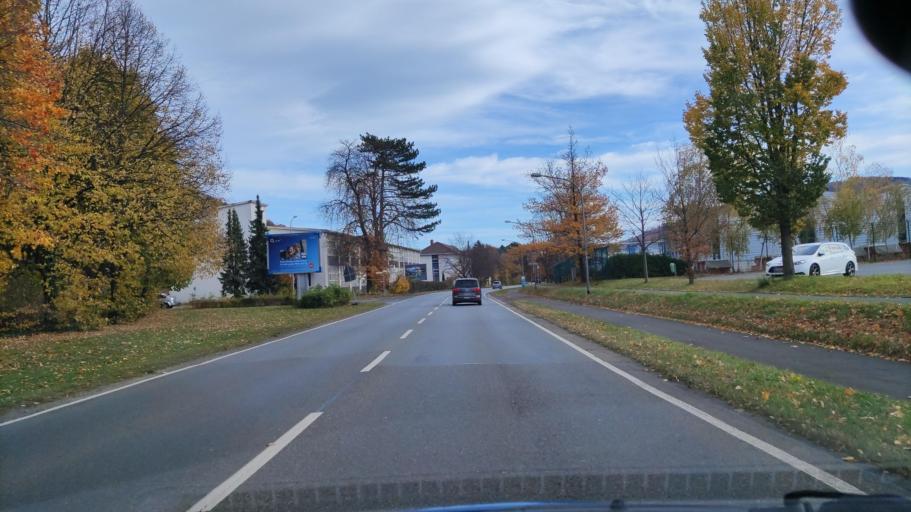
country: DE
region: Lower Saxony
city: Goslar
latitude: 51.9123
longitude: 10.4624
